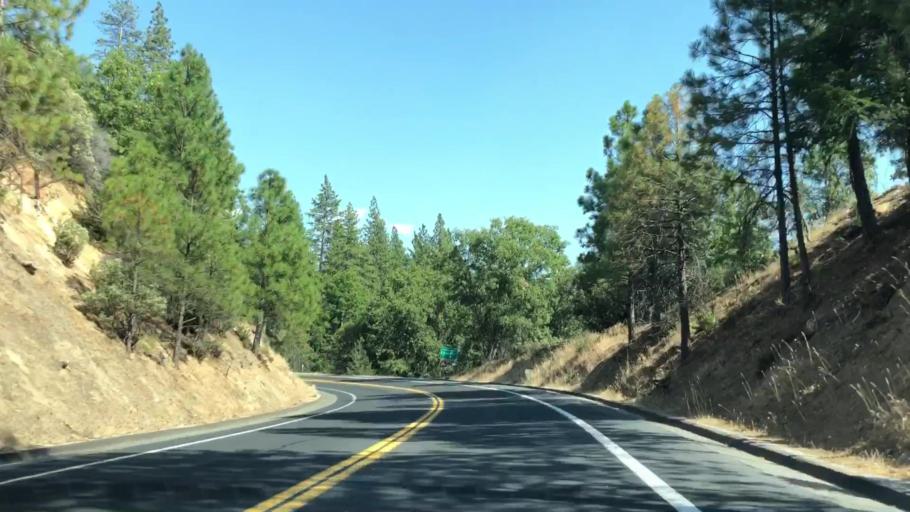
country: US
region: California
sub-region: Mariposa County
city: Midpines
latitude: 37.8162
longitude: -119.9416
